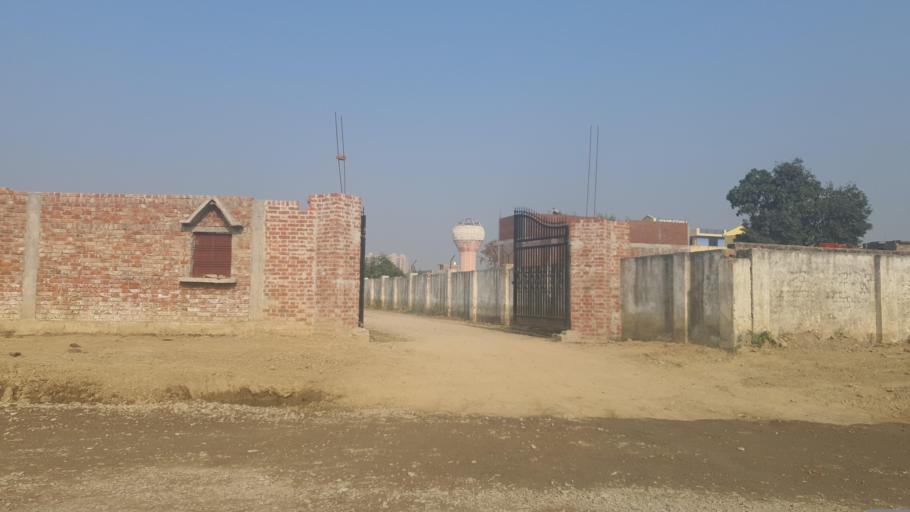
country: IN
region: Uttar Pradesh
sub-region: Lucknow District
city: Goshainganj
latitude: 26.7727
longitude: 81.0098
